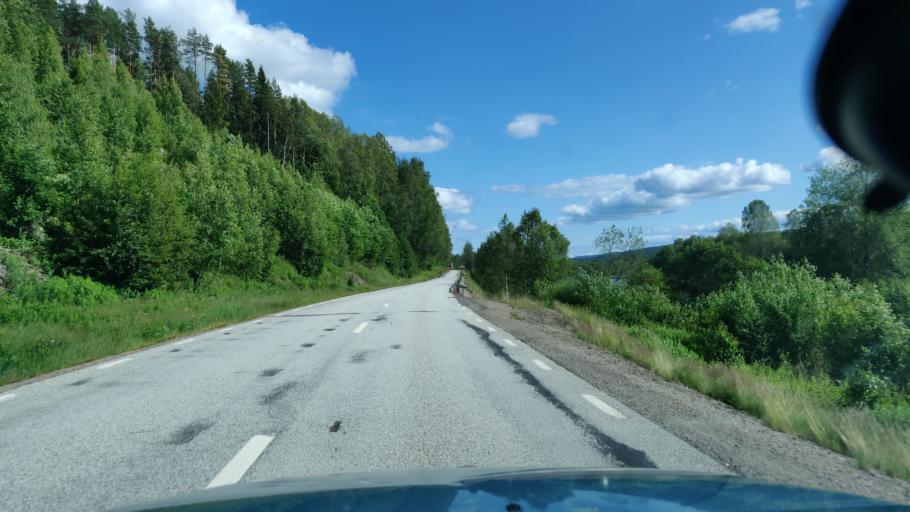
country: SE
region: Vaermland
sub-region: Torsby Kommun
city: Torsby
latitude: 60.4729
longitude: 13.1975
